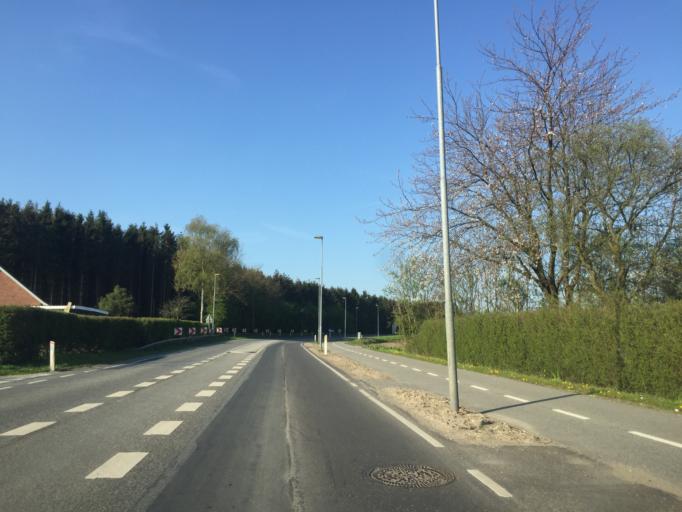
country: DK
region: South Denmark
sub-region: Svendborg Kommune
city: Thuro By
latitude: 55.0850
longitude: 10.6865
